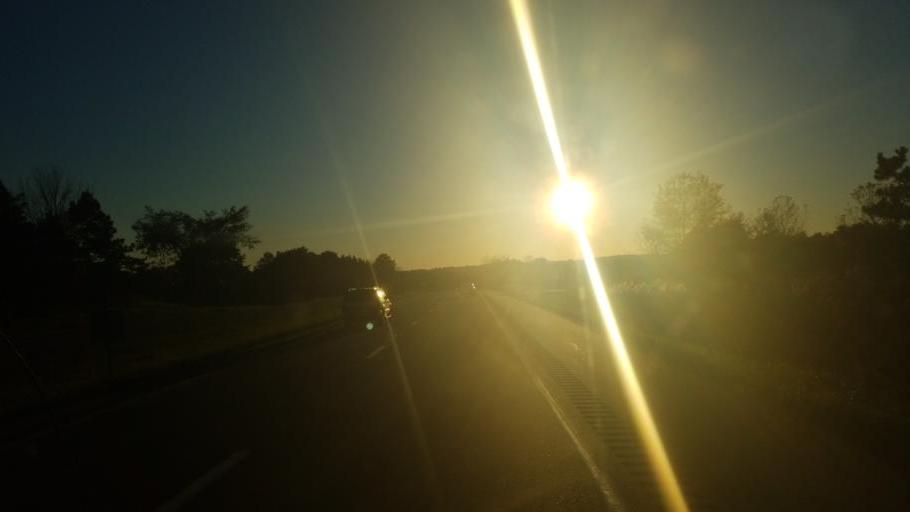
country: US
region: Ohio
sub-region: Stark County
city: Louisville
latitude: 40.8788
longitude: -81.2270
